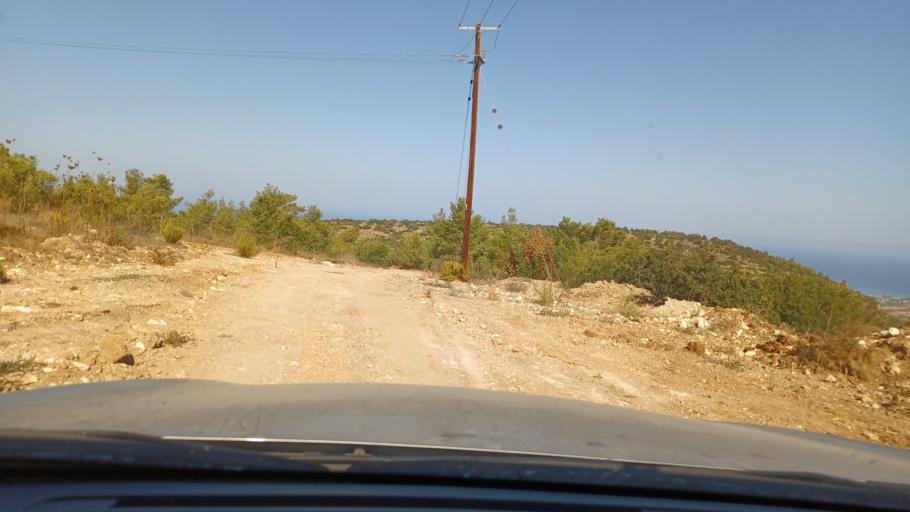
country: CY
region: Pafos
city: Polis
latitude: 35.0133
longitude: 32.4836
